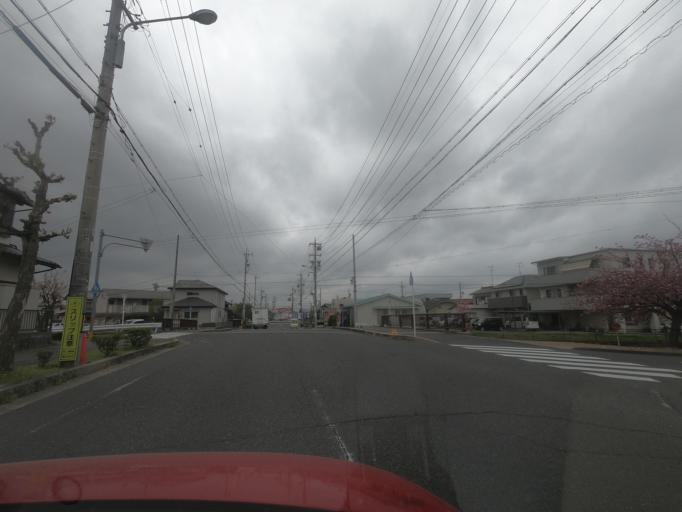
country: JP
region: Aichi
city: Kasugai
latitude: 35.2639
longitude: 136.9547
